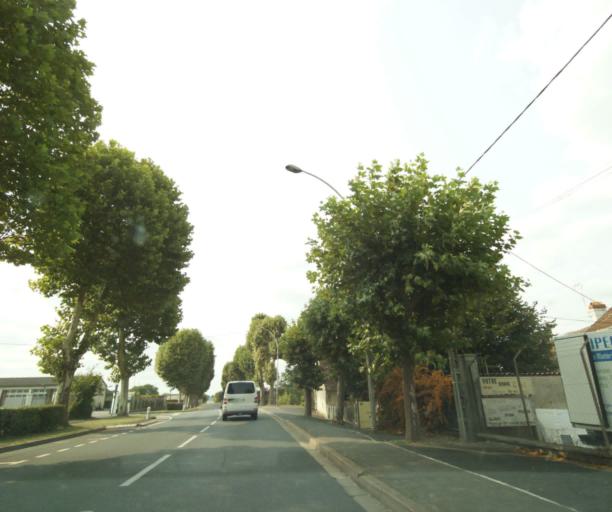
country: FR
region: Centre
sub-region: Departement de l'Indre
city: Chatillon-sur-Indre
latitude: 46.9942
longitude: 1.1626
